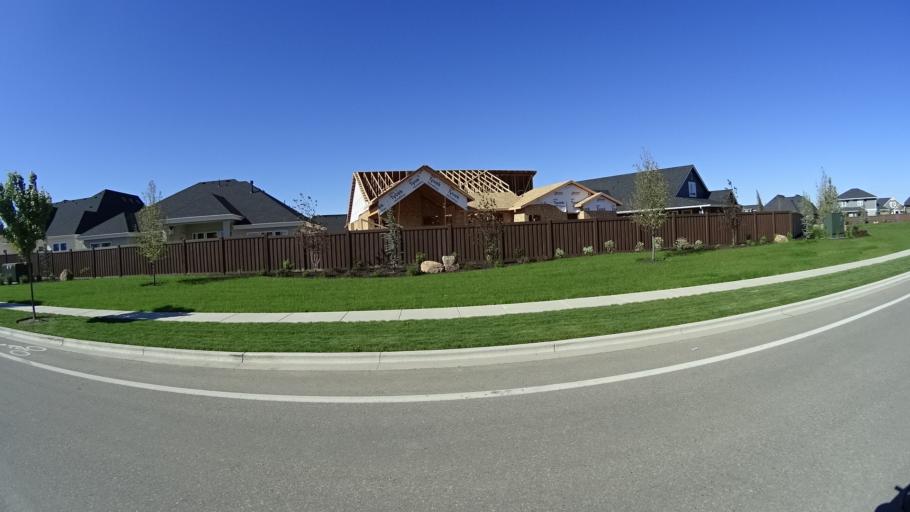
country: US
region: Idaho
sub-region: Ada County
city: Meridian
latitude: 43.6592
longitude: -116.4368
